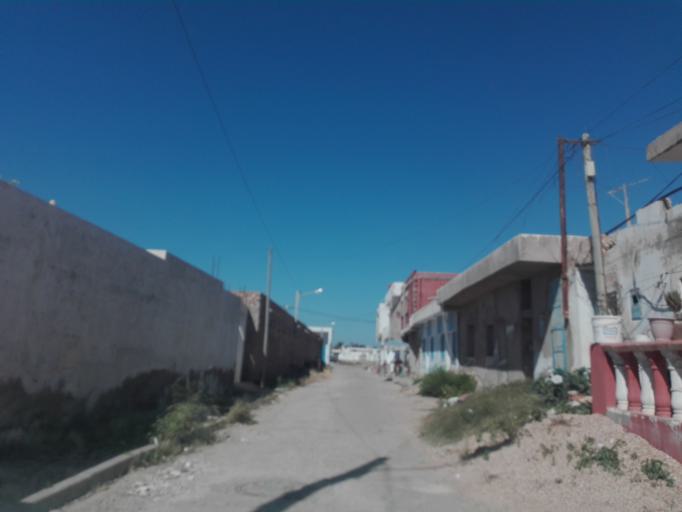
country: TN
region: Safaqis
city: Al Qarmadah
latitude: 34.7064
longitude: 11.1995
